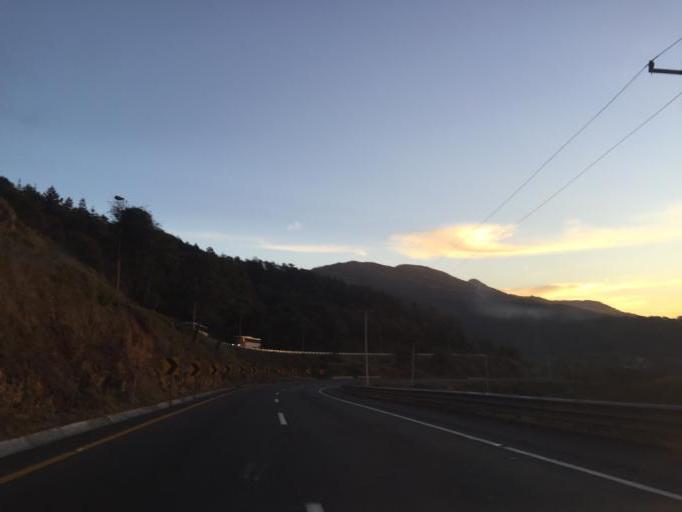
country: MX
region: Veracruz
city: Maltrata
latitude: 18.8511
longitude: -97.2716
